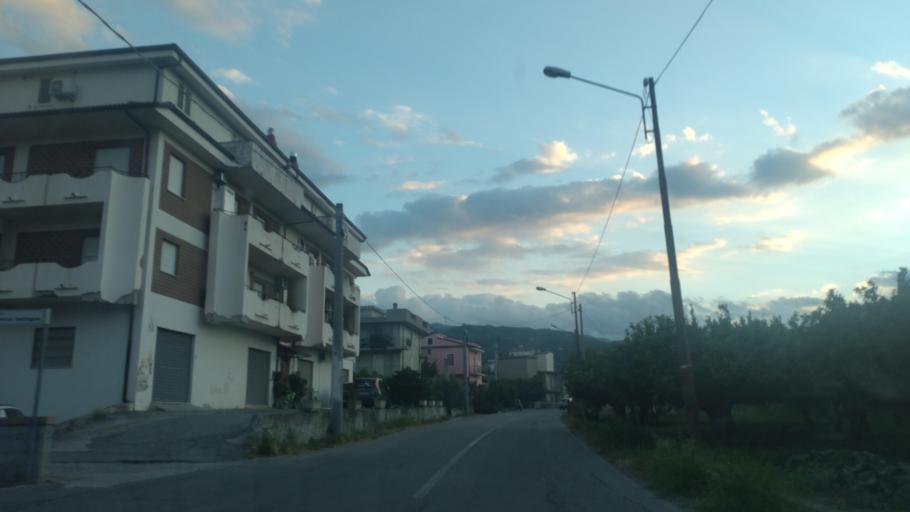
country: IT
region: Calabria
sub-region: Provincia di Catanzaro
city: Marina di Davoli
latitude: 38.6673
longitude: 16.5404
